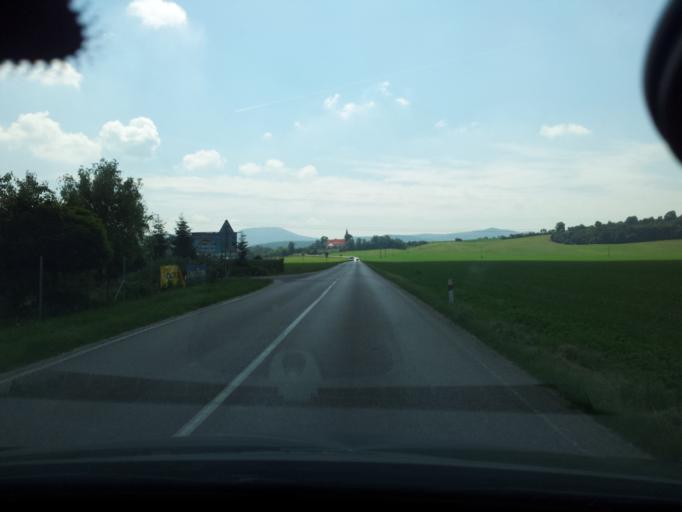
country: SK
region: Nitriansky
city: Partizanske
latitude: 48.6236
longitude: 18.4283
